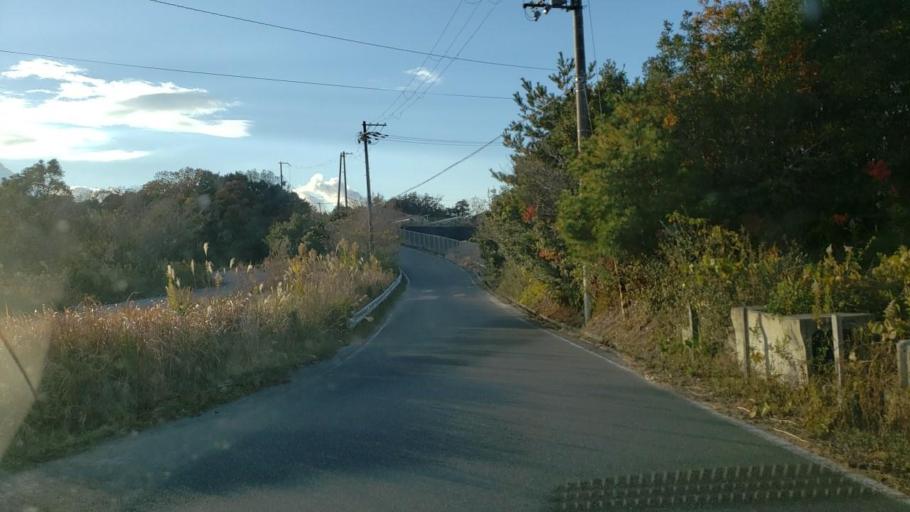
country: JP
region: Hyogo
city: Akashi
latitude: 34.5392
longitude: 134.9602
